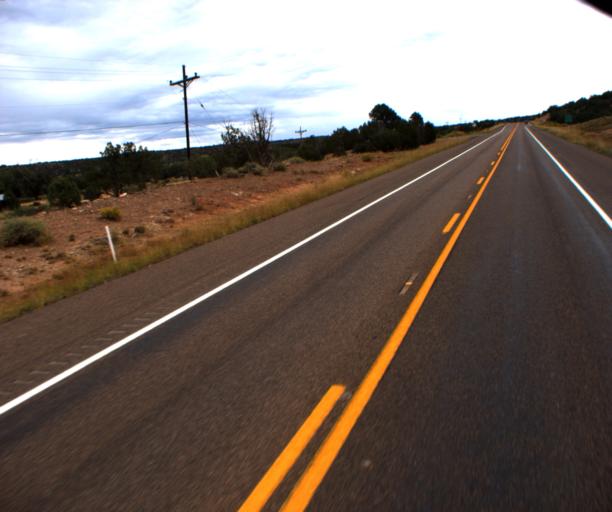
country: US
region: Arizona
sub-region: Navajo County
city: White Mountain Lake
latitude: 34.3890
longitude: -110.0634
